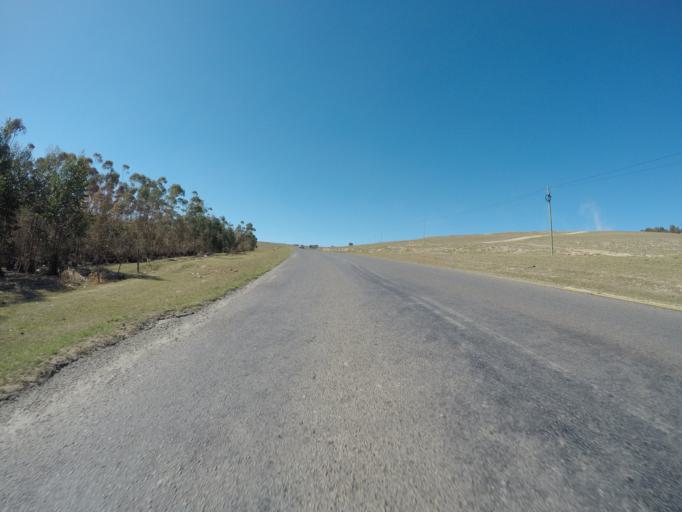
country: ZA
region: Eastern Cape
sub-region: OR Tambo District Municipality
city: Mthatha
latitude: -31.7781
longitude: 28.7372
